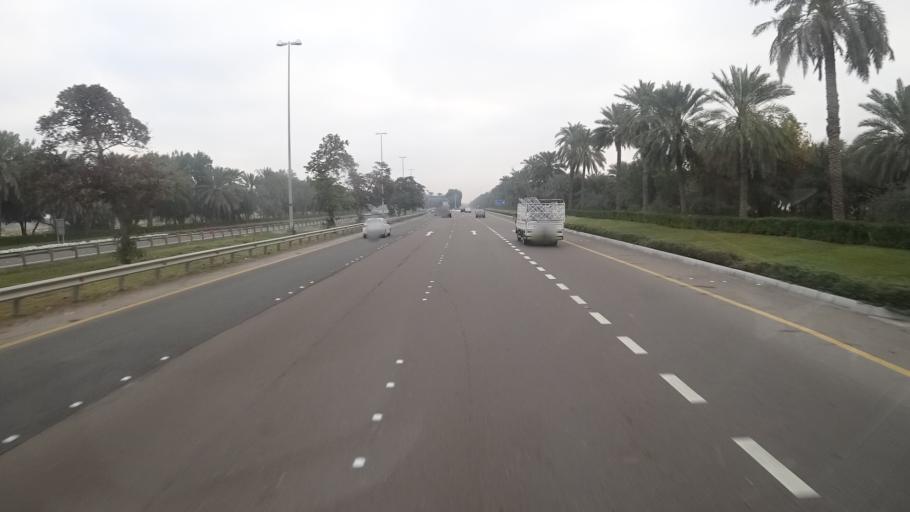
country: AE
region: Abu Dhabi
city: Abu Dhabi
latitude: 24.4070
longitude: 54.6220
